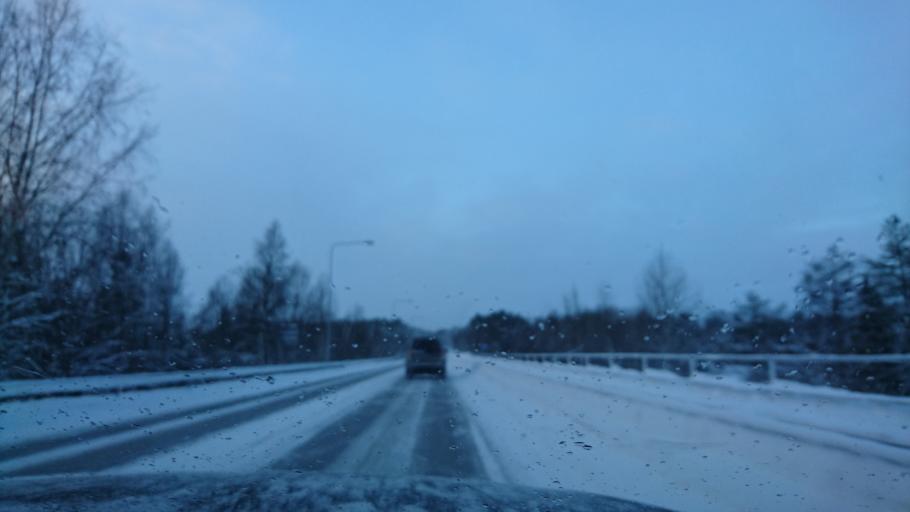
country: FI
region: Northern Ostrobothnia
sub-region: Koillismaa
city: Taivalkoski
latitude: 65.5697
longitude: 28.2405
